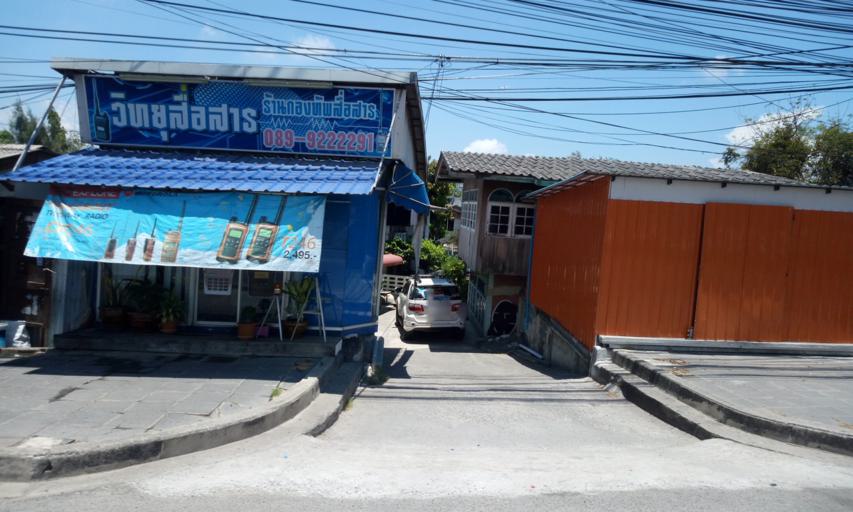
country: TH
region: Bangkok
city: Bang Na
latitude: 13.6320
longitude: 100.7085
